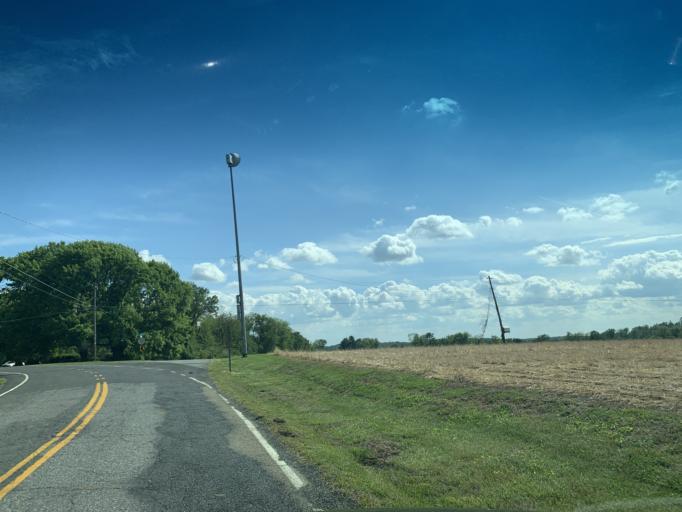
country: US
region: Maryland
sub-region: Cecil County
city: Rising Sun
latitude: 39.7087
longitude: -76.2030
